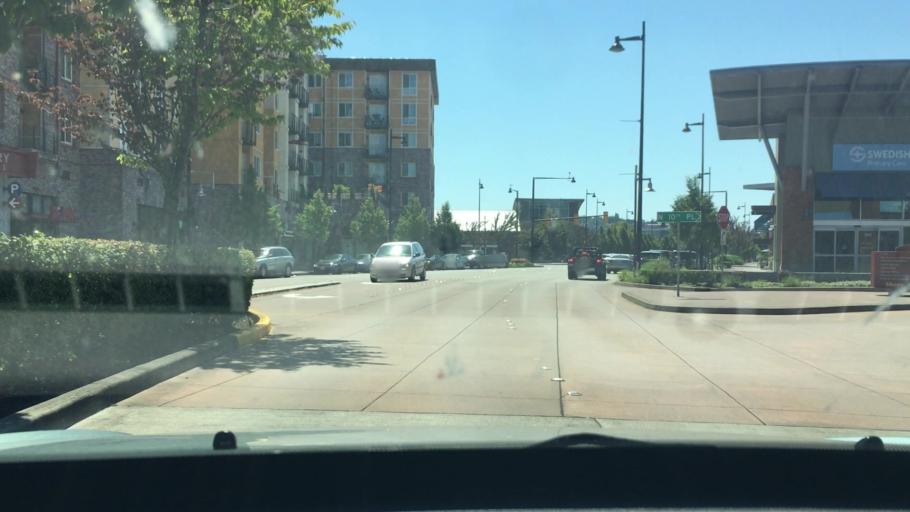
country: US
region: Washington
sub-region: King County
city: Renton
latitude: 47.4991
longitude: -122.2025
